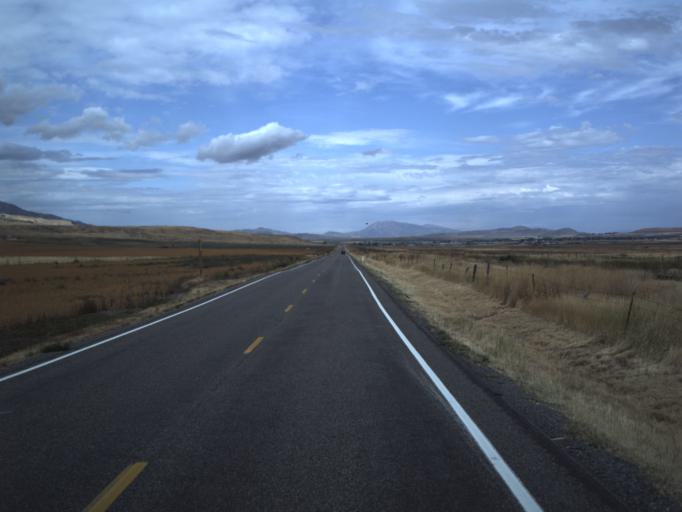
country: US
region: Utah
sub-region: Cache County
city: Benson
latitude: 41.7903
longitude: -111.9885
